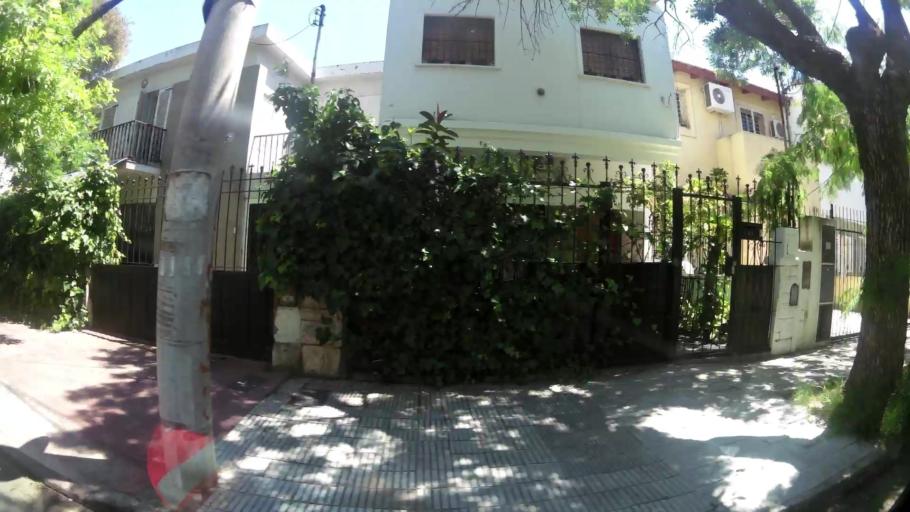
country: AR
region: Cordoba
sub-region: Departamento de Capital
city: Cordoba
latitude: -31.4121
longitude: -64.2033
